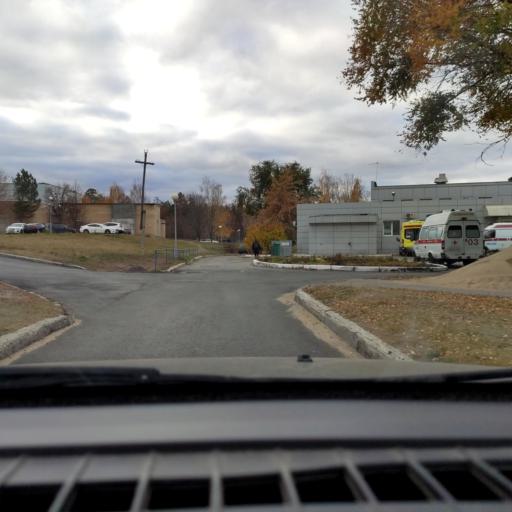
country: RU
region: Samara
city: Tol'yatti
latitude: 53.5218
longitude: 49.3256
